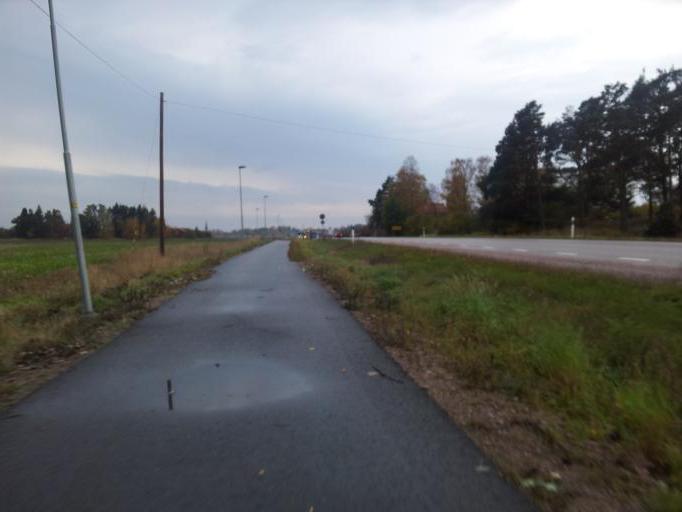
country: SE
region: Uppsala
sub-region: Uppsala Kommun
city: Gamla Uppsala
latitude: 59.8936
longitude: 17.7029
